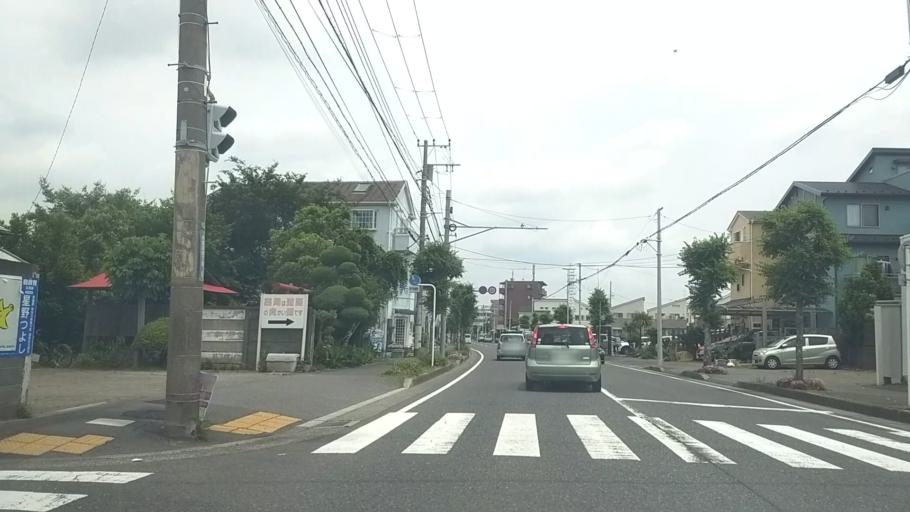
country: JP
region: Kanagawa
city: Fujisawa
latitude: 35.3317
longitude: 139.4709
